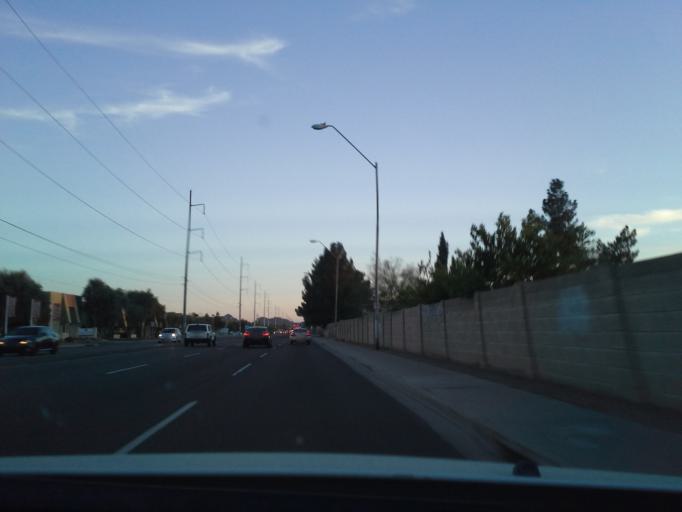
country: US
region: Arizona
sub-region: Maricopa County
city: Glendale
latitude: 33.6458
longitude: -112.0657
